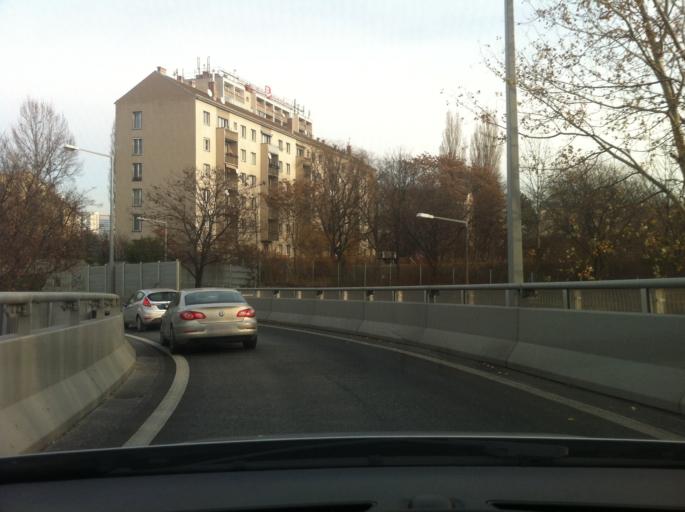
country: AT
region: Vienna
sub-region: Wien Stadt
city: Vienna
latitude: 48.2356
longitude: 16.3625
